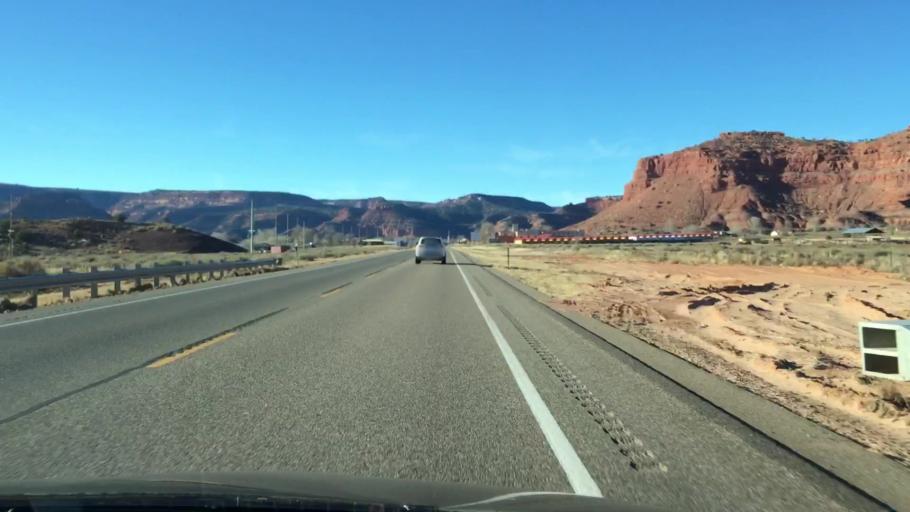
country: US
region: Utah
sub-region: Kane County
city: Kanab
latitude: 37.0378
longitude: -112.5044
